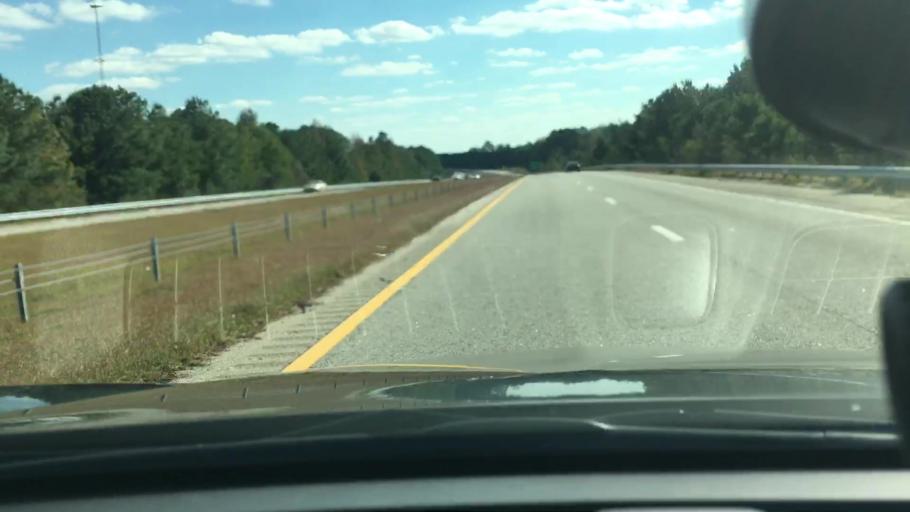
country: US
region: North Carolina
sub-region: Wilson County
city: Lucama
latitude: 35.7504
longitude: -78.0231
